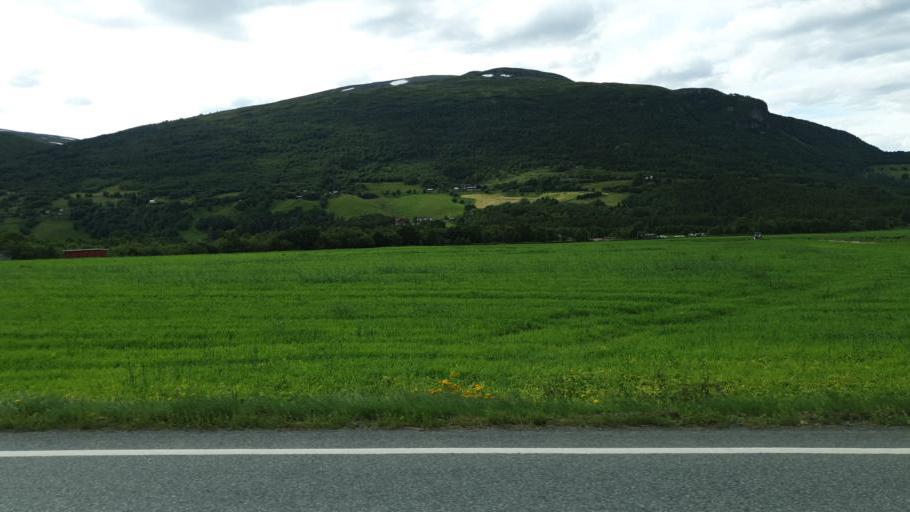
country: NO
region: Sor-Trondelag
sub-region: Oppdal
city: Oppdal
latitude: 62.5366
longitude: 9.6254
